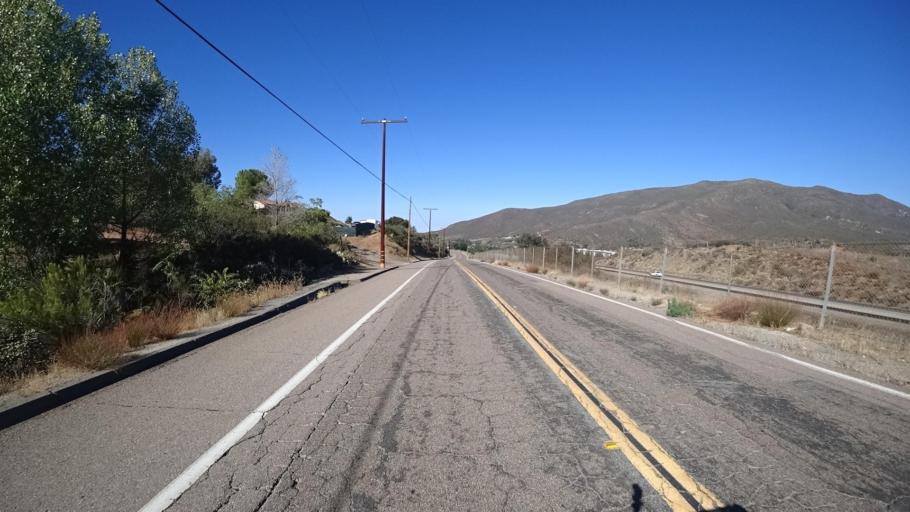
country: US
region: California
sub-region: San Diego County
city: Alpine
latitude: 32.8383
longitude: -116.6982
